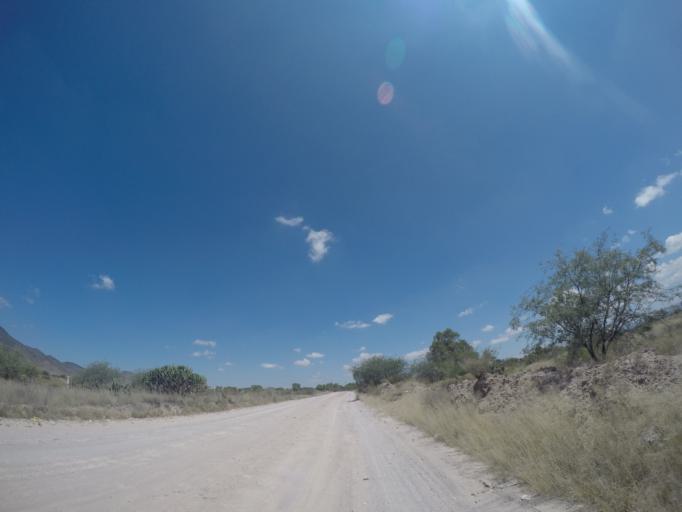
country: MX
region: San Luis Potosi
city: La Pila
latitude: 21.9937
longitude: -100.8989
